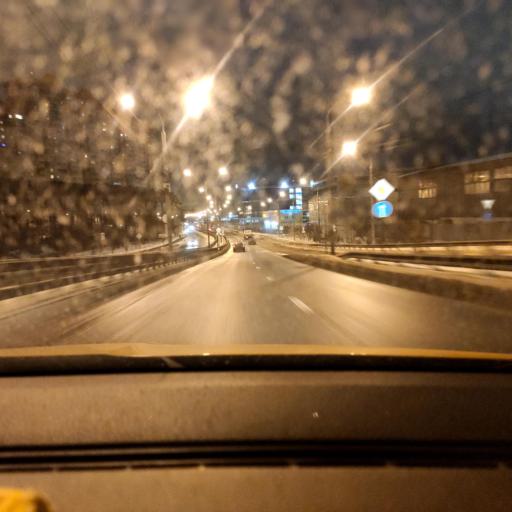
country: RU
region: Moskovskaya
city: Odintsovo
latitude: 55.6674
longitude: 37.2799
